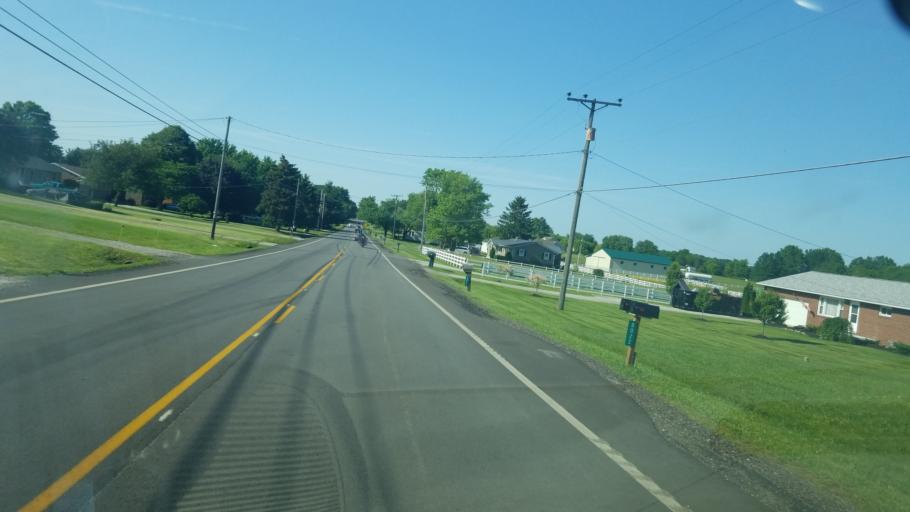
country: US
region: Ohio
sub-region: Wayne County
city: Smithville
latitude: 40.8967
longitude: -81.9155
